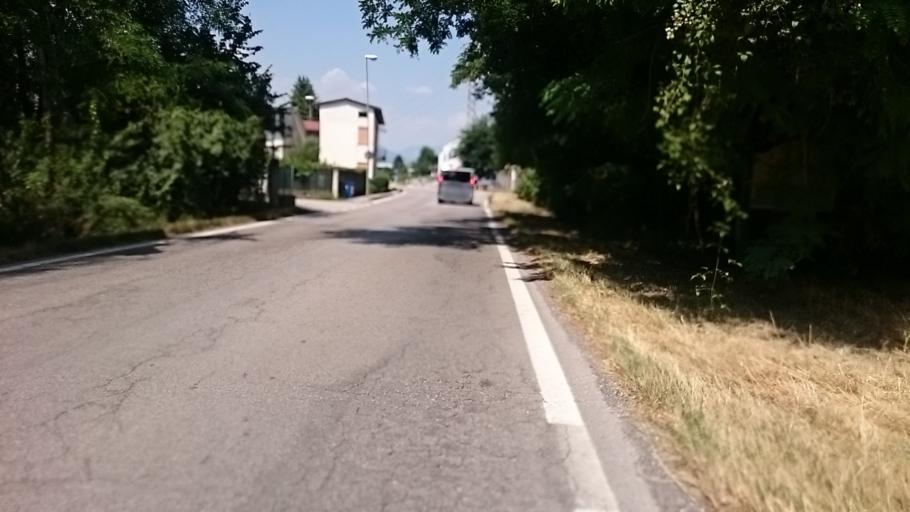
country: IT
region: Veneto
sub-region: Provincia di Vicenza
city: Rosa
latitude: 45.6920
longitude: 11.7397
